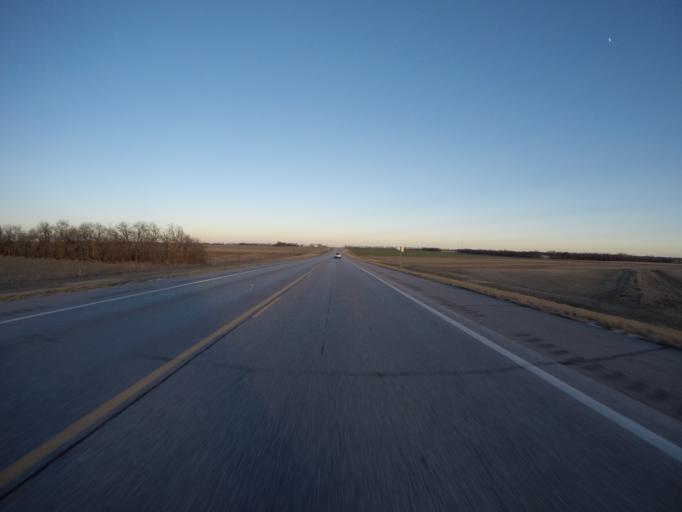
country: US
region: Kansas
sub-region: Marion County
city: Peabody
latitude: 38.1747
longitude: -97.1587
